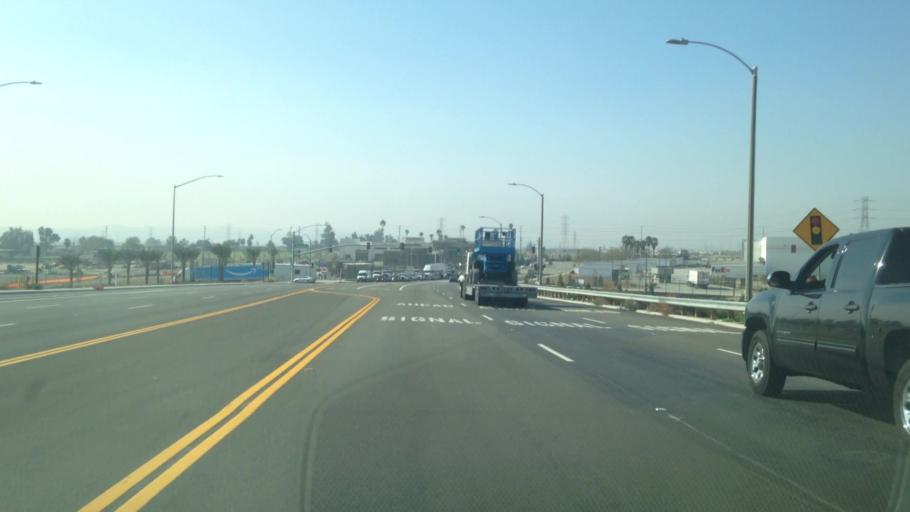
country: US
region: California
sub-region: Riverside County
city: Mira Loma
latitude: 34.0016
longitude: -117.5527
